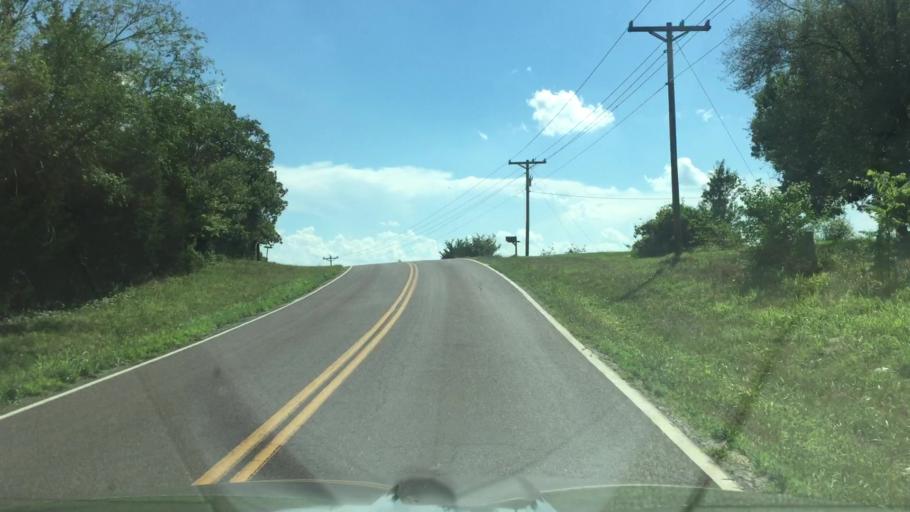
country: US
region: Missouri
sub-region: Miller County
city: Tuscumbia
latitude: 38.1244
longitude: -92.4657
